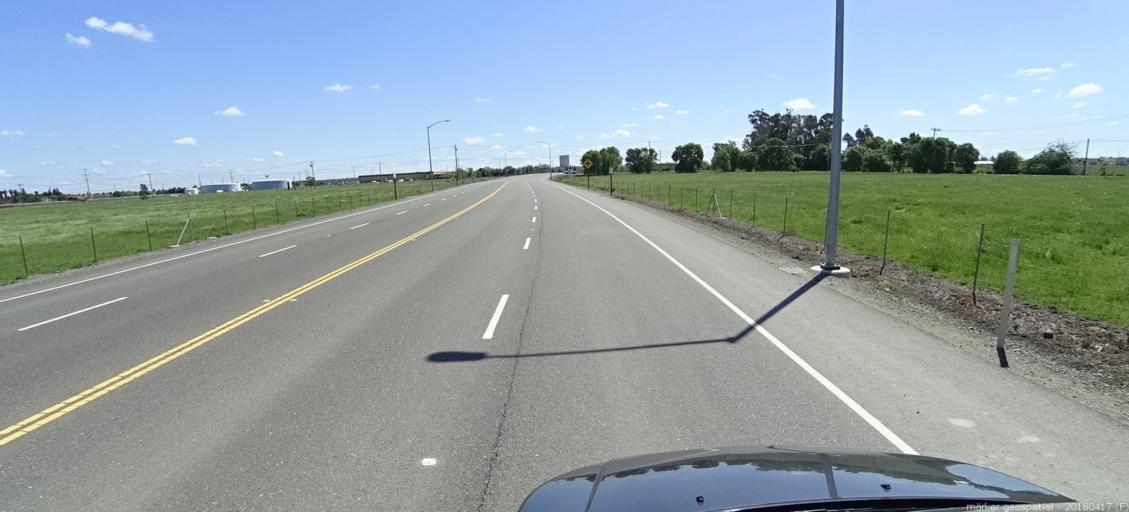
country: US
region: California
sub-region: Sacramento County
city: Laguna
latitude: 38.4361
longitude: -121.4630
